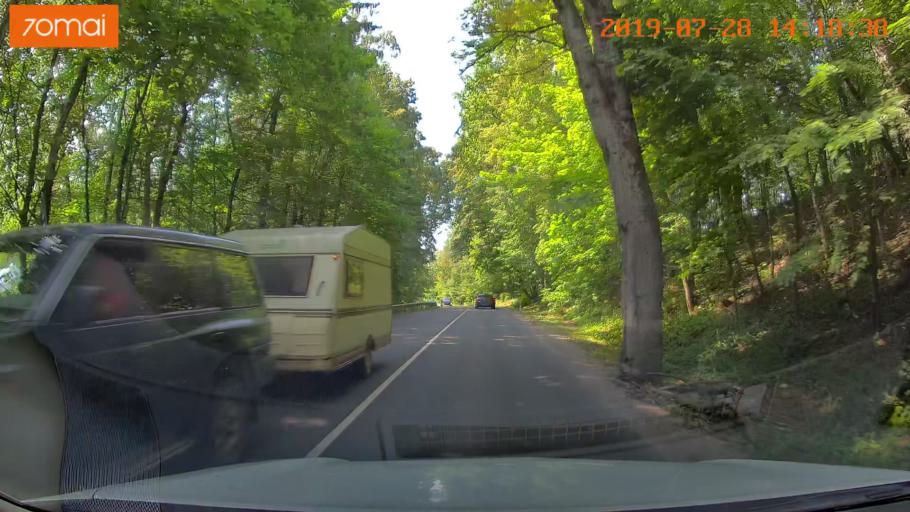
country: RU
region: Kaliningrad
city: Volochayevskoye
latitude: 54.8180
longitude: 20.2373
